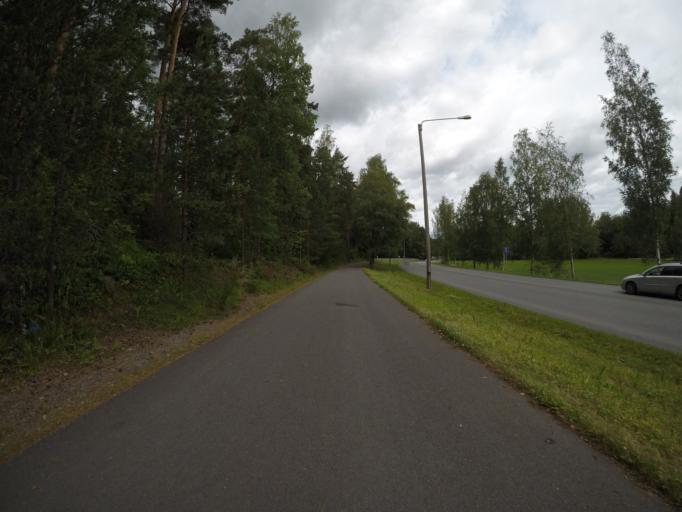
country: FI
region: Haeme
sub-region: Haemeenlinna
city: Haemeenlinna
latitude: 60.9702
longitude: 24.4370
